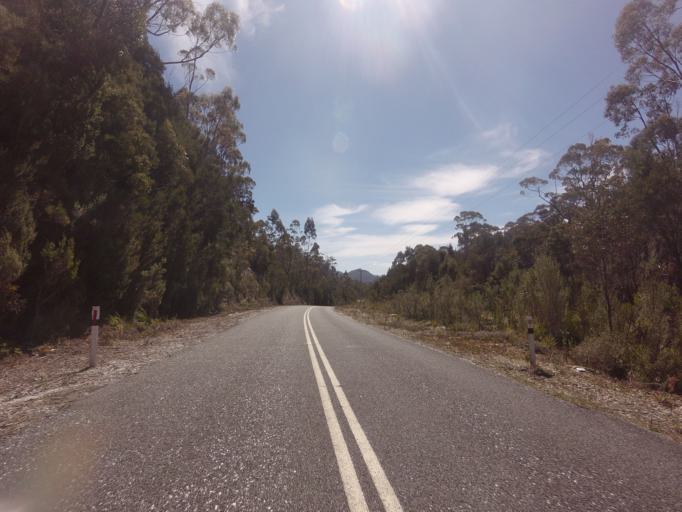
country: AU
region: Tasmania
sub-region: West Coast
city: Queenstown
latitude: -42.7630
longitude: 146.0053
